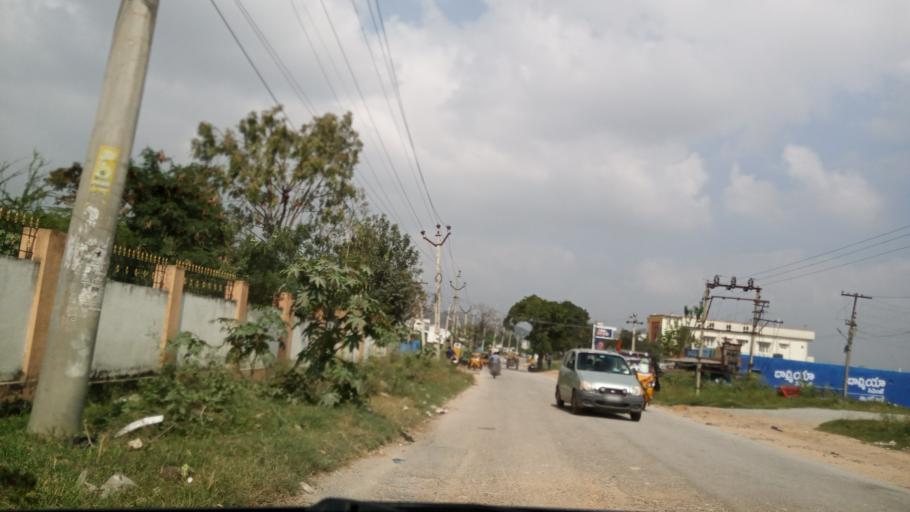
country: IN
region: Andhra Pradesh
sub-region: Chittoor
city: Madanapalle
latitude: 13.5681
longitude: 78.5145
